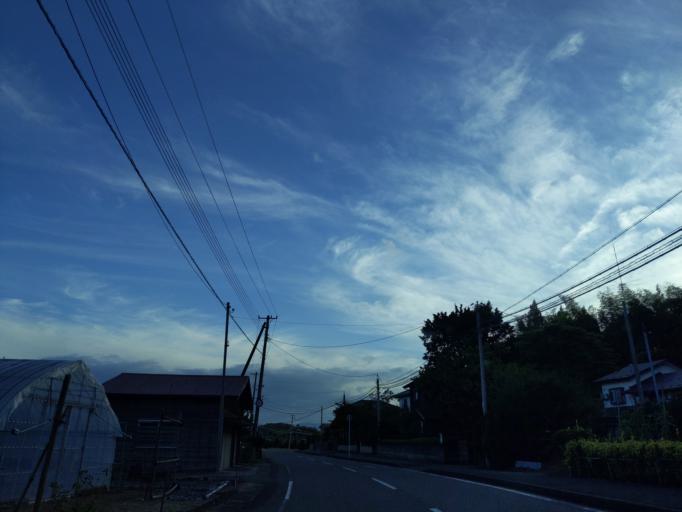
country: JP
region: Niigata
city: Kashiwazaki
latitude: 37.4342
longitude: 138.6228
